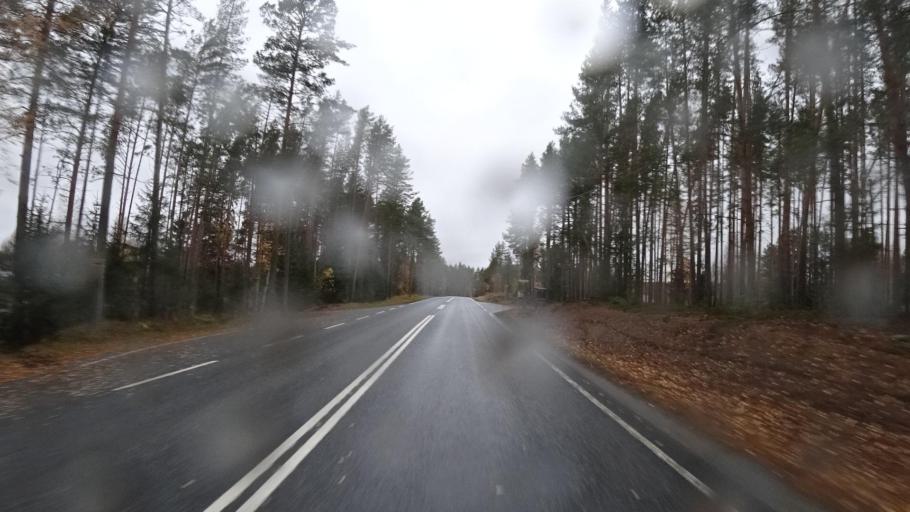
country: FI
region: Northern Savo
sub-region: Koillis-Savo
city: Juankoski
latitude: 62.8766
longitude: 28.2969
